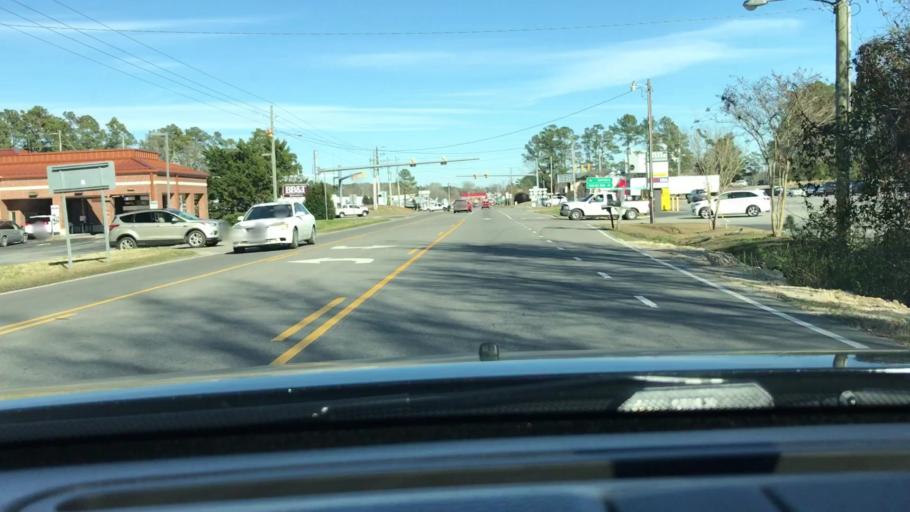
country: US
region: North Carolina
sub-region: Brunswick County
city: Shallotte
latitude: 33.9681
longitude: -78.3919
